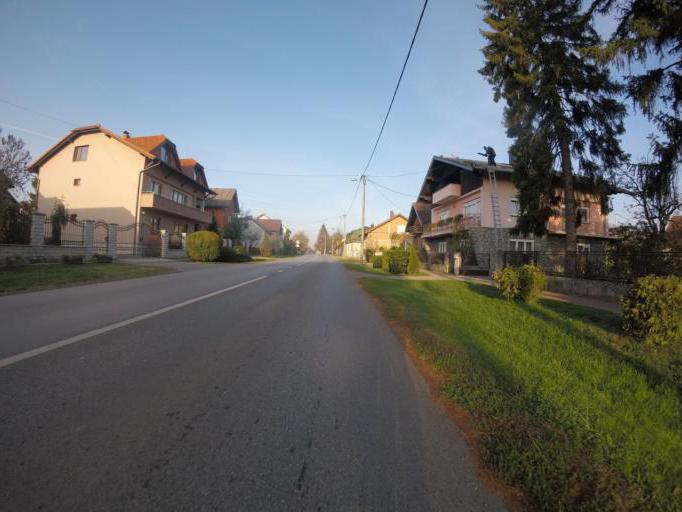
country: HR
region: Zagrebacka
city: Kuce
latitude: 45.7033
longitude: 16.1233
